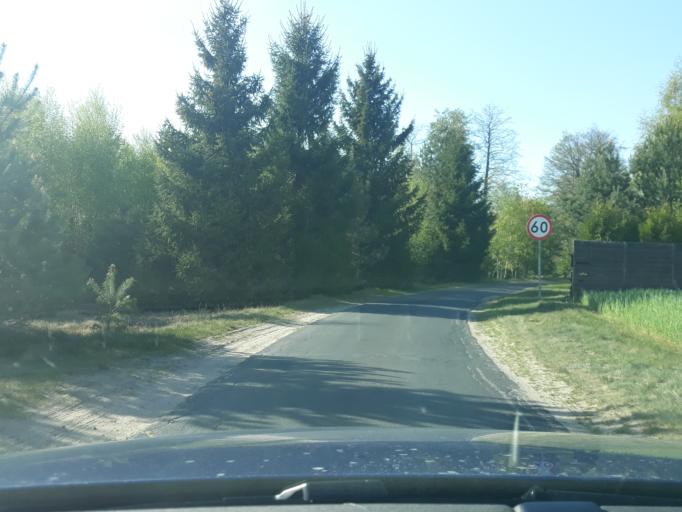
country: PL
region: Pomeranian Voivodeship
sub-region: Powiat czluchowski
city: Przechlewo
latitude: 53.8784
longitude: 17.3231
